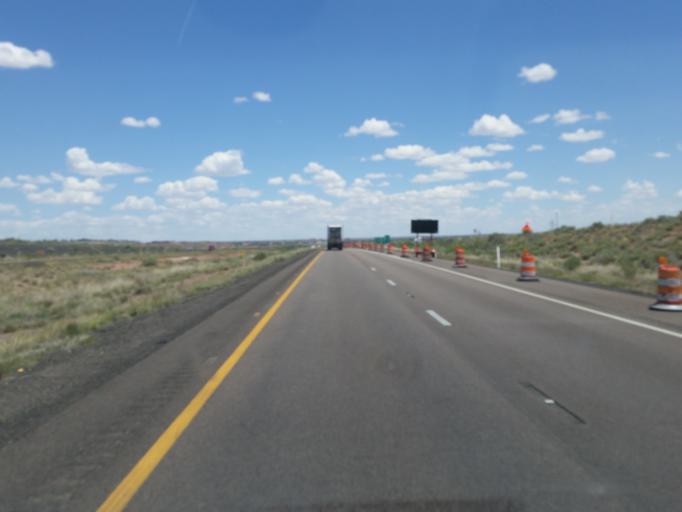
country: US
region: Arizona
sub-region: Navajo County
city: Holbrook
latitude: 34.9072
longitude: -110.2120
